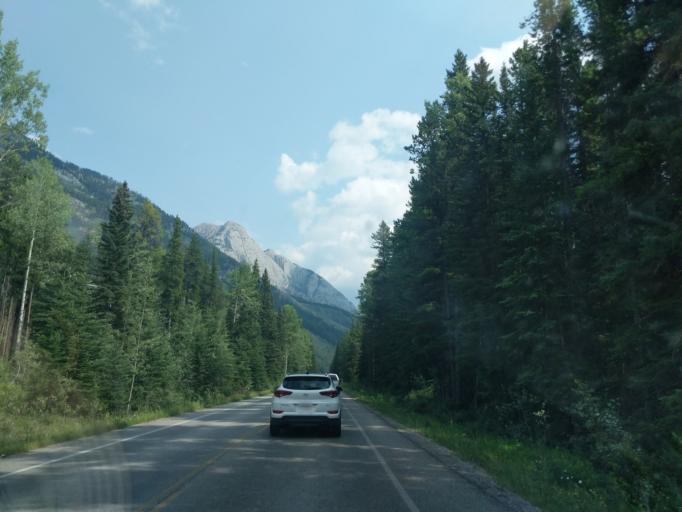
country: CA
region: Alberta
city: Banff
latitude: 51.1942
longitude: -115.7408
